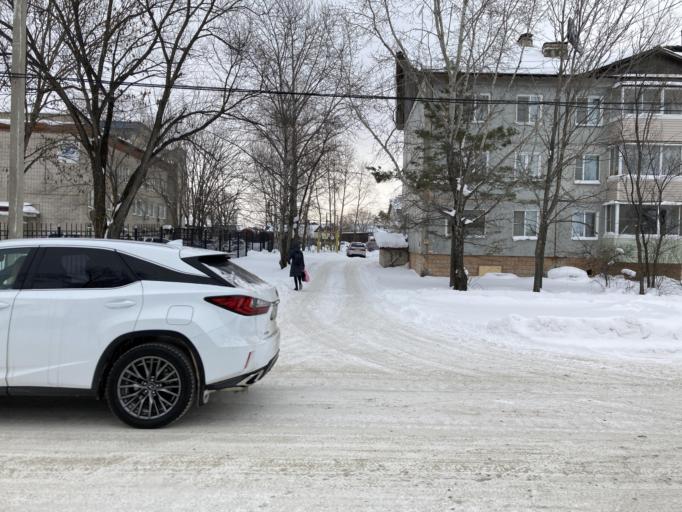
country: RU
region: Khabarovsk Krai
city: Khor
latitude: 47.9725
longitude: 135.0539
